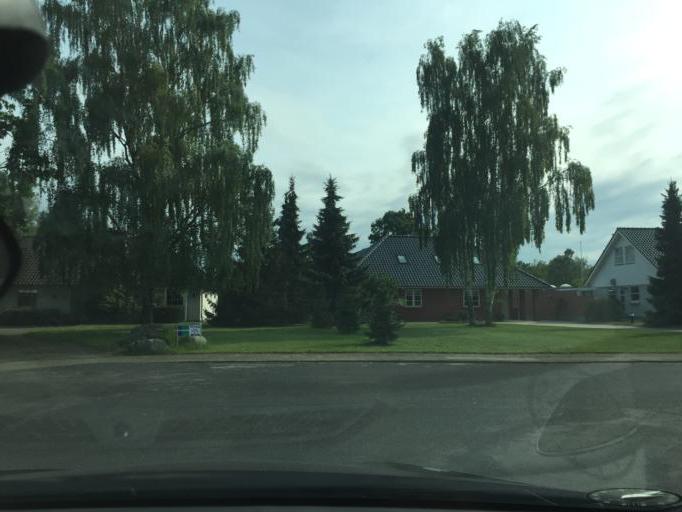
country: DK
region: South Denmark
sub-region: Odense Kommune
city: Bellinge
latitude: 55.3311
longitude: 10.3207
